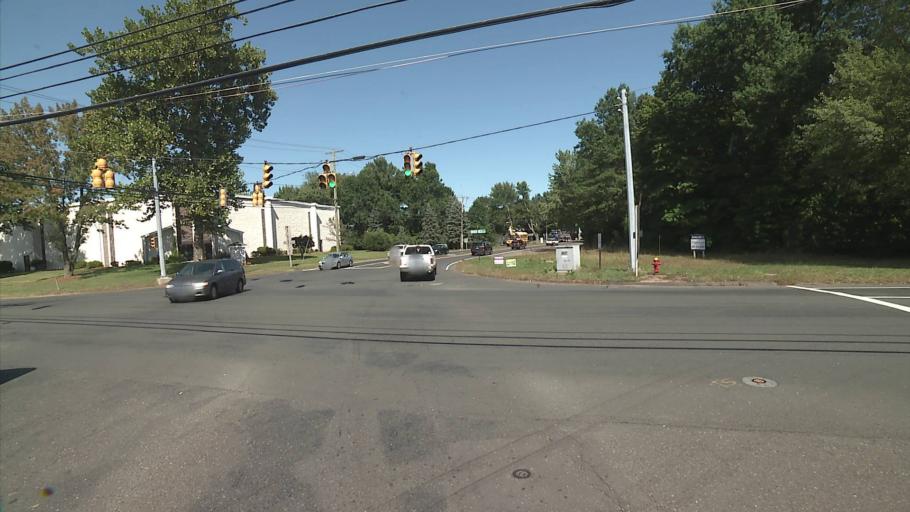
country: US
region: Connecticut
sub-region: Hartford County
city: Blue Hills
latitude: 41.8352
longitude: -72.6988
